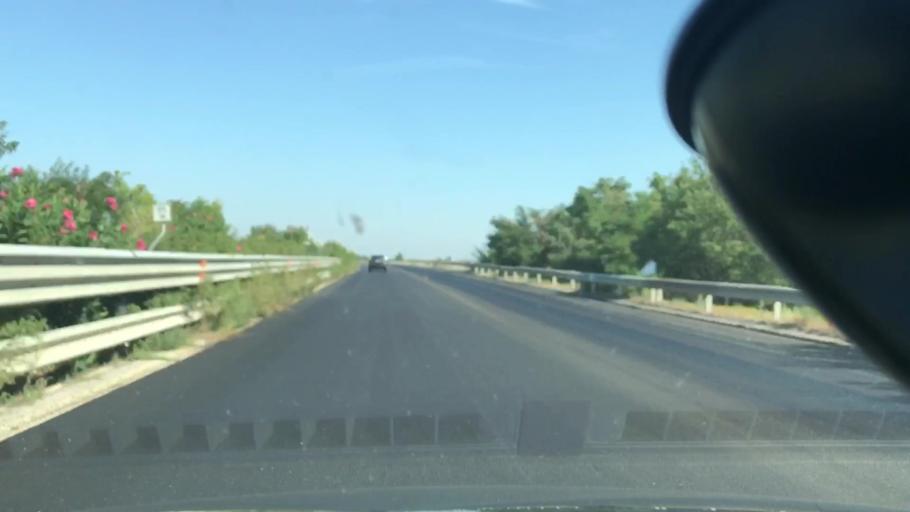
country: IT
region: Apulia
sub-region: Provincia di Foggia
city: Ascoli Satriano
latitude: 41.2750
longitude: 15.5534
